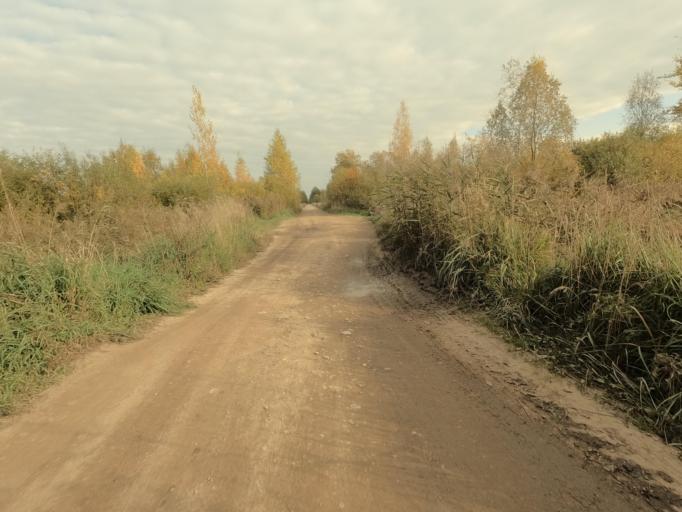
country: RU
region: Novgorod
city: Pankovka
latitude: 58.8967
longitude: 31.0026
